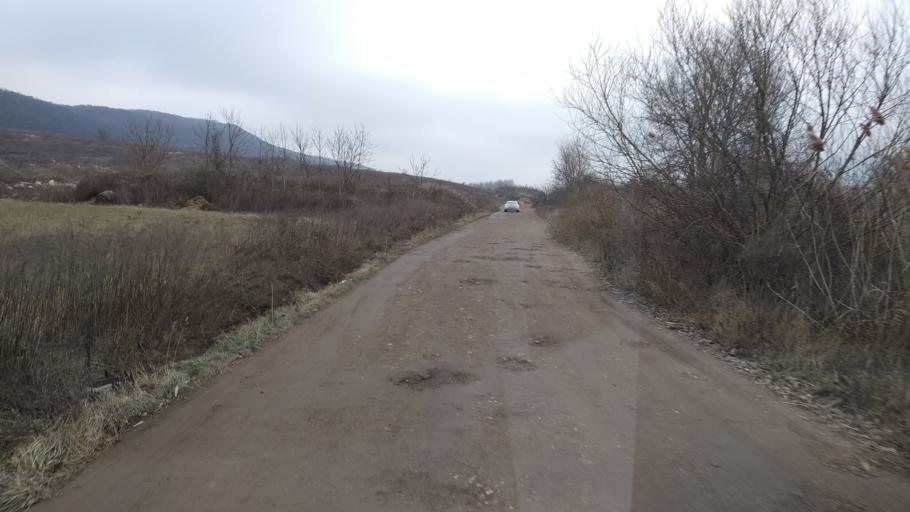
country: HU
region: Pest
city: Pilisborosjeno
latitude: 47.6039
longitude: 18.9658
